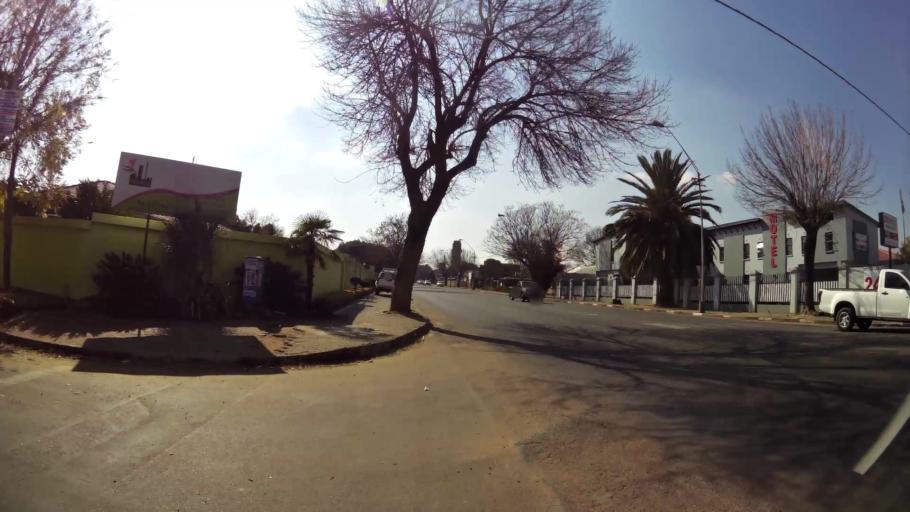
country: ZA
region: Gauteng
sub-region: City of Johannesburg Metropolitan Municipality
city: Modderfontein
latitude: -26.1002
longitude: 28.2332
